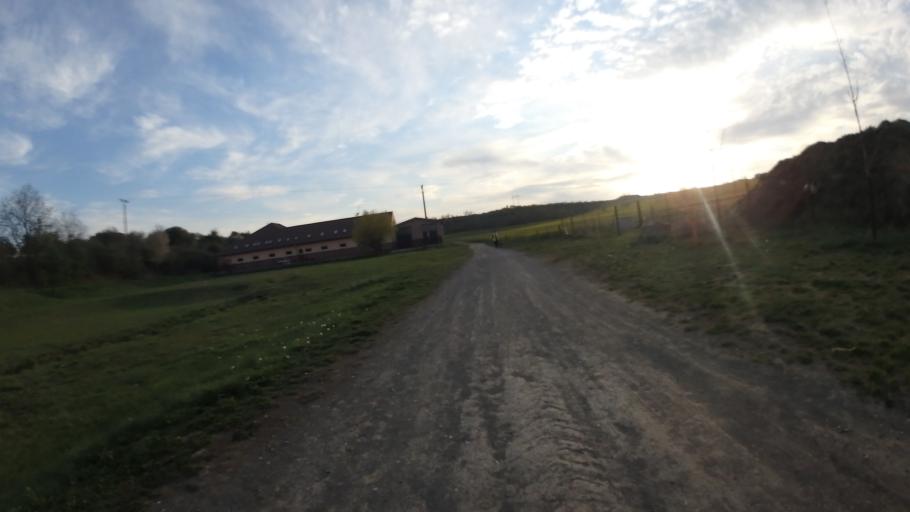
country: CZ
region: South Moravian
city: Moravany
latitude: 49.1436
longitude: 16.5735
